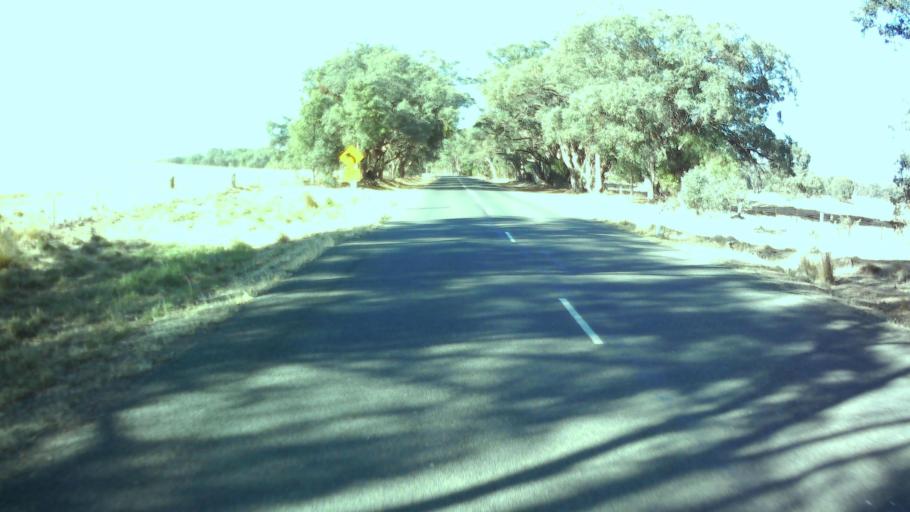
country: AU
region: New South Wales
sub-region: Weddin
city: Grenfell
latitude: -33.9918
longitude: 148.1356
